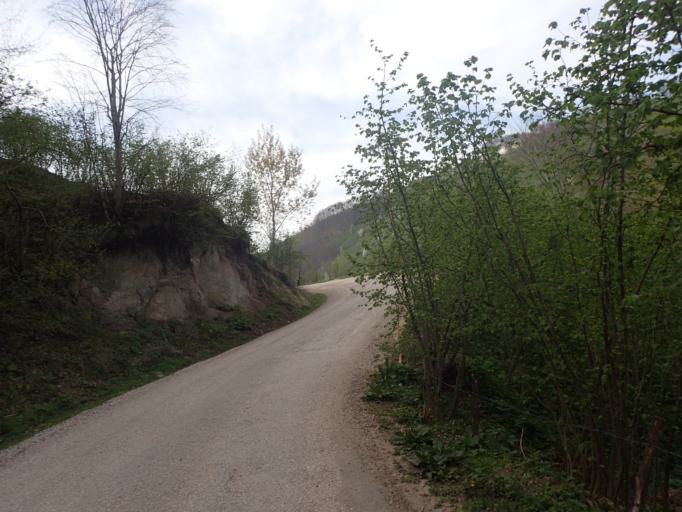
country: TR
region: Ordu
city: Aybasti
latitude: 40.7106
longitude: 37.2796
